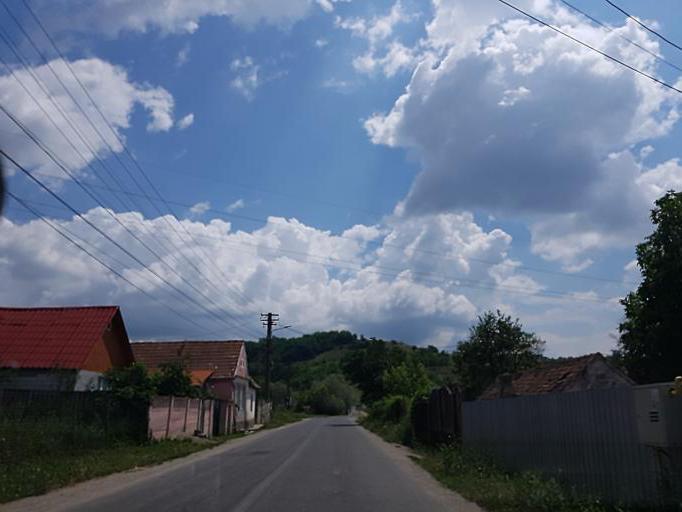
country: RO
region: Sibiu
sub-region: Comuna Seica Mica
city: Seica Mica
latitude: 46.0523
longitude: 24.1426
